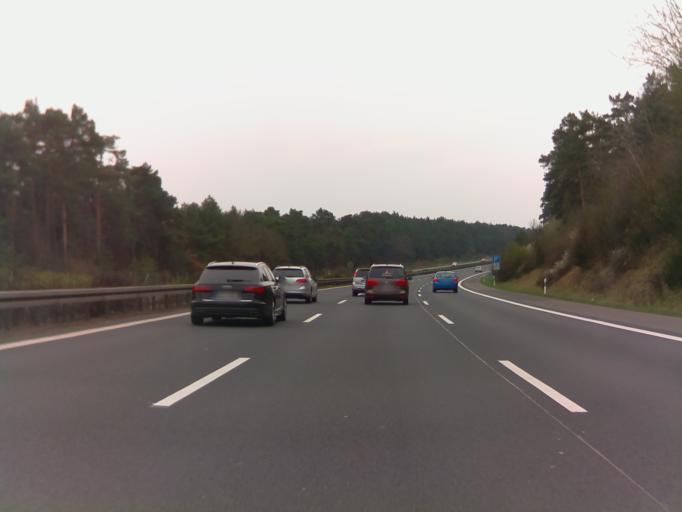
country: DE
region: Brandenburg
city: Beelitz
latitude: 52.2349
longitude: 12.9171
